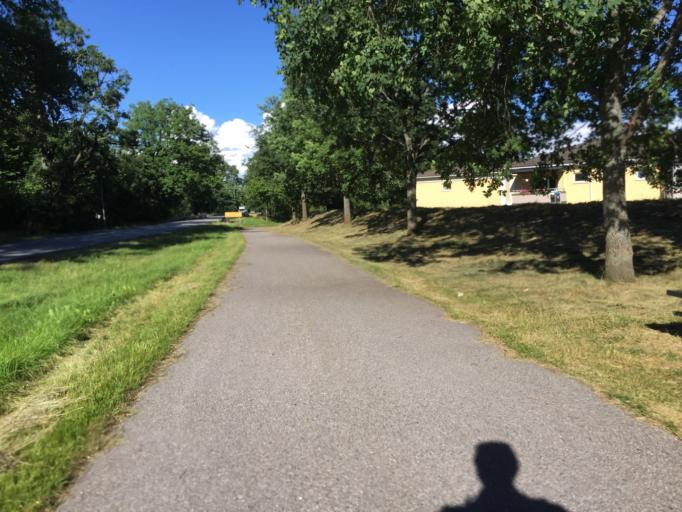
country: SE
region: OErebro
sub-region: Orebro Kommun
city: Orebro
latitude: 59.2740
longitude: 15.1507
